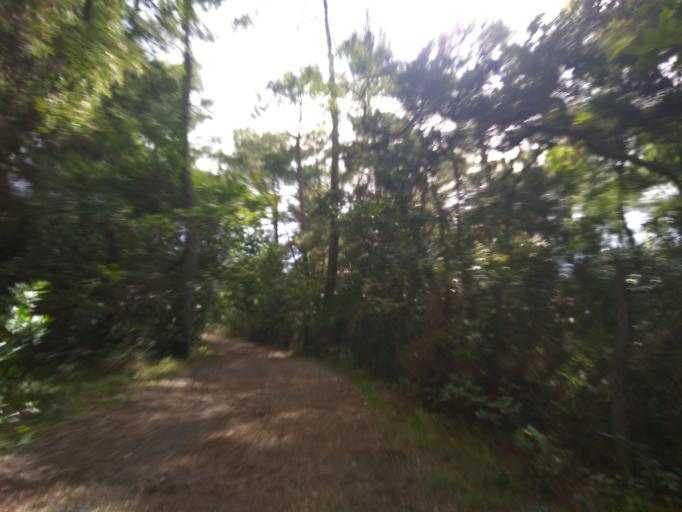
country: FR
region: Aquitaine
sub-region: Departement des Landes
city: Capbreton
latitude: 43.6302
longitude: -1.4430
